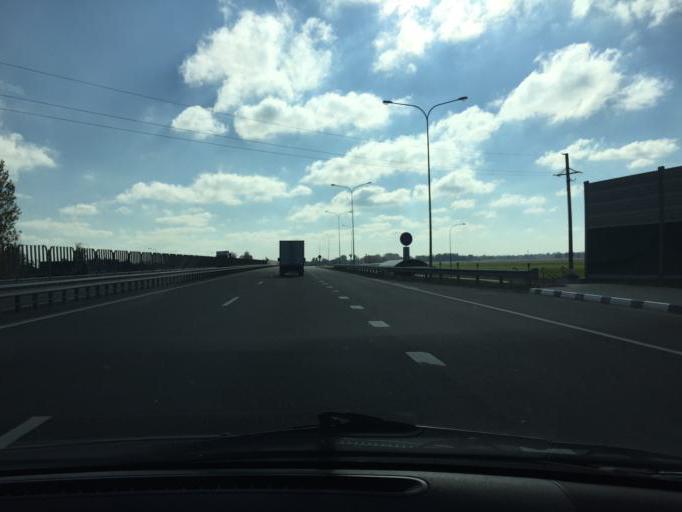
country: BY
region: Minsk
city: Slutsk
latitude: 53.1048
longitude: 27.5693
